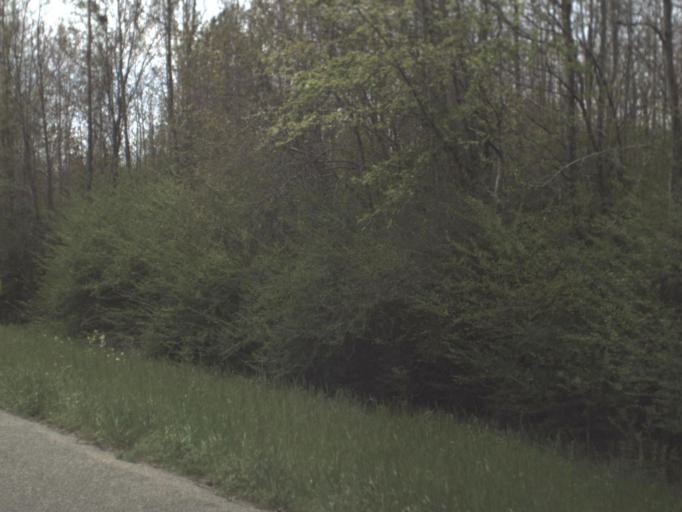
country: US
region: Florida
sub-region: Jackson County
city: Graceville
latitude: 30.8721
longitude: -85.5263
